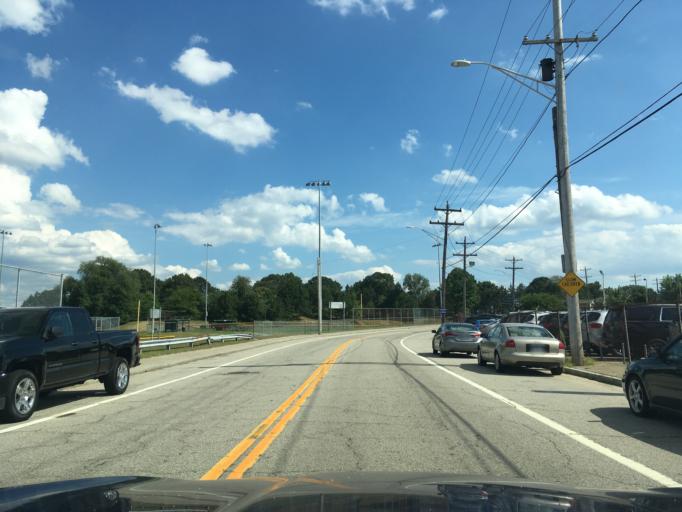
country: US
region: Rhode Island
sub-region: Providence County
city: Cranston
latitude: 41.7938
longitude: -71.4382
